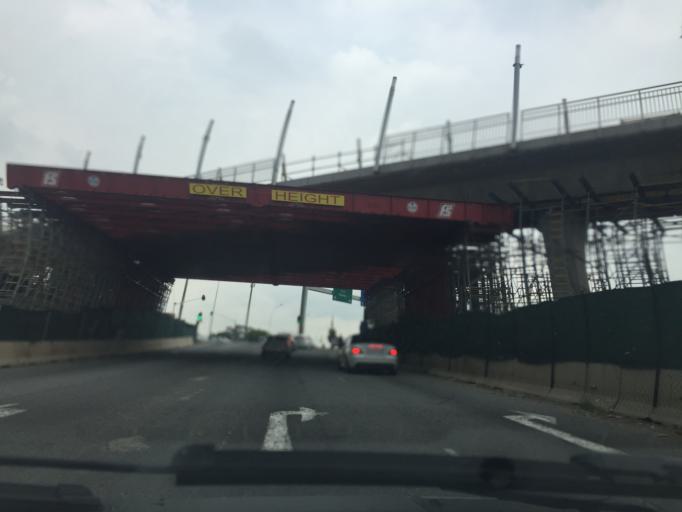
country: ZA
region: Gauteng
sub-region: City of Johannesburg Metropolitan Municipality
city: Modderfontein
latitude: -26.1079
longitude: 28.0772
